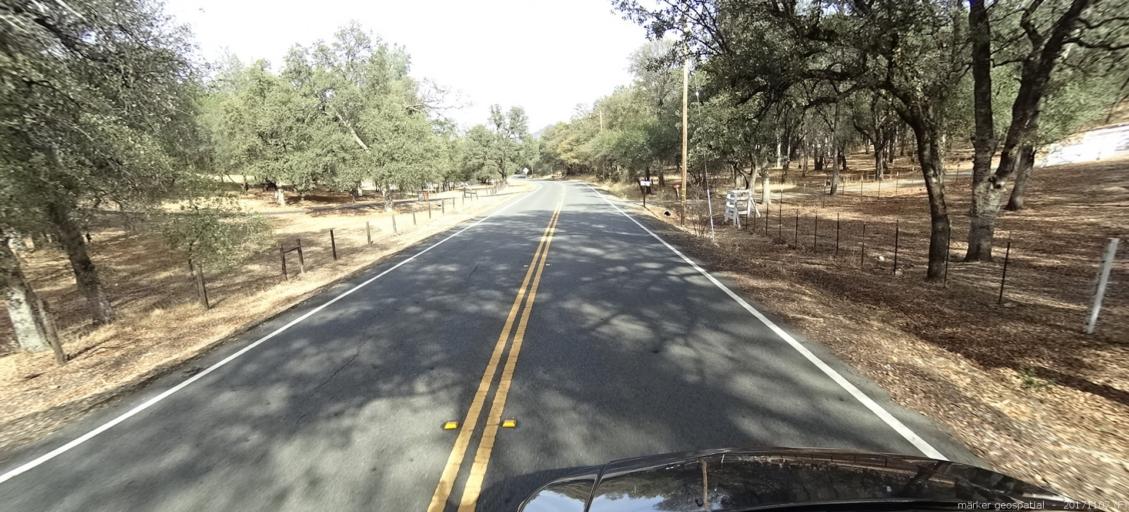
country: US
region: California
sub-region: Shasta County
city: Shasta
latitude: 40.4907
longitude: -122.5494
